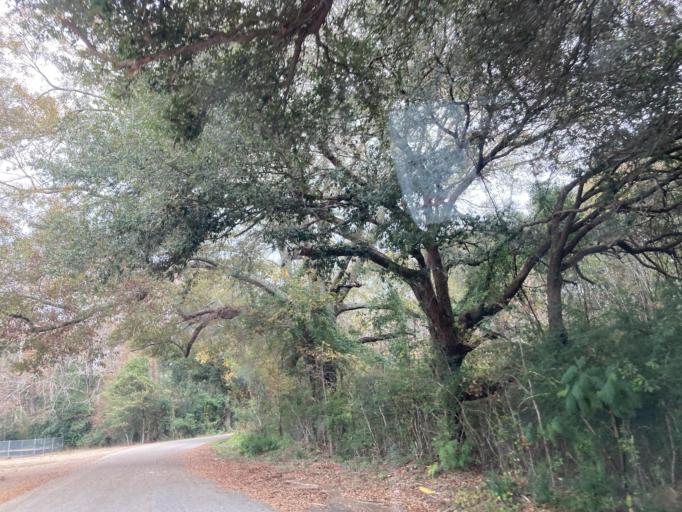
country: US
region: Mississippi
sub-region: Lamar County
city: Lumberton
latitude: 31.0612
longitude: -89.6218
